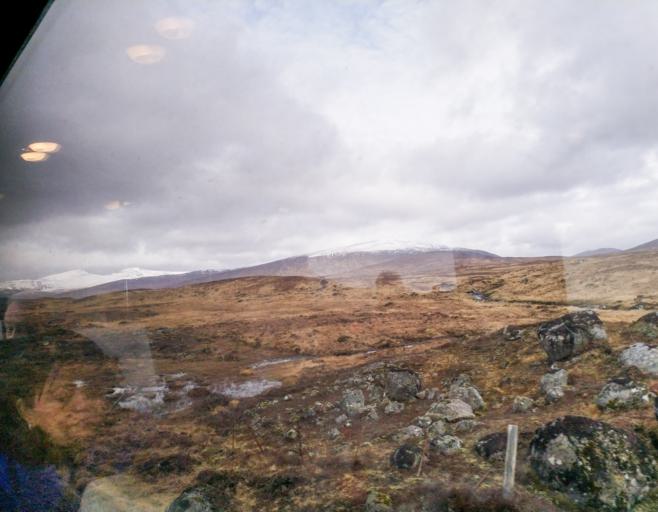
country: GB
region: Scotland
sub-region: Highland
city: Spean Bridge
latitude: 56.7303
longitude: -4.6487
